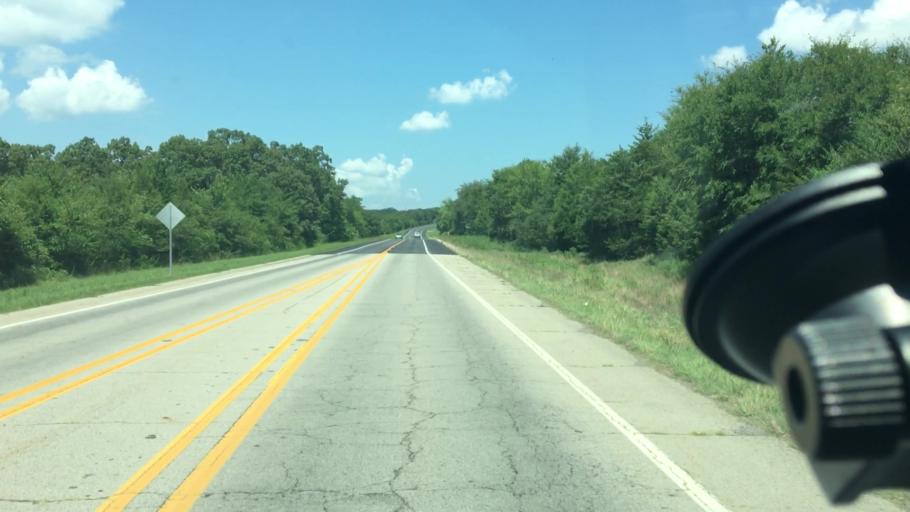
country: US
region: Arkansas
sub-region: Sebastian County
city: Lavaca
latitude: 35.2971
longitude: -94.1499
